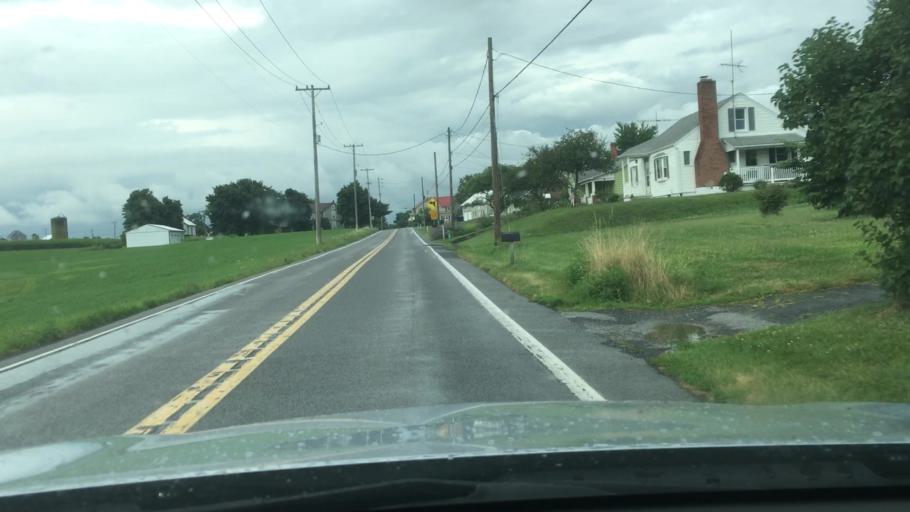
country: US
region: Pennsylvania
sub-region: Franklin County
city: Chambersburg
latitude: 39.8870
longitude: -77.7242
